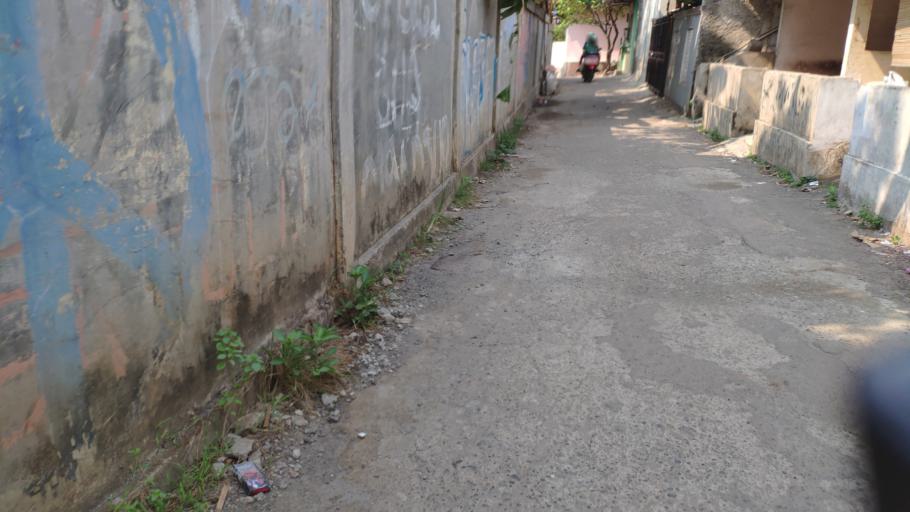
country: ID
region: West Java
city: Pamulang
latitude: -6.3135
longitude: 106.8102
